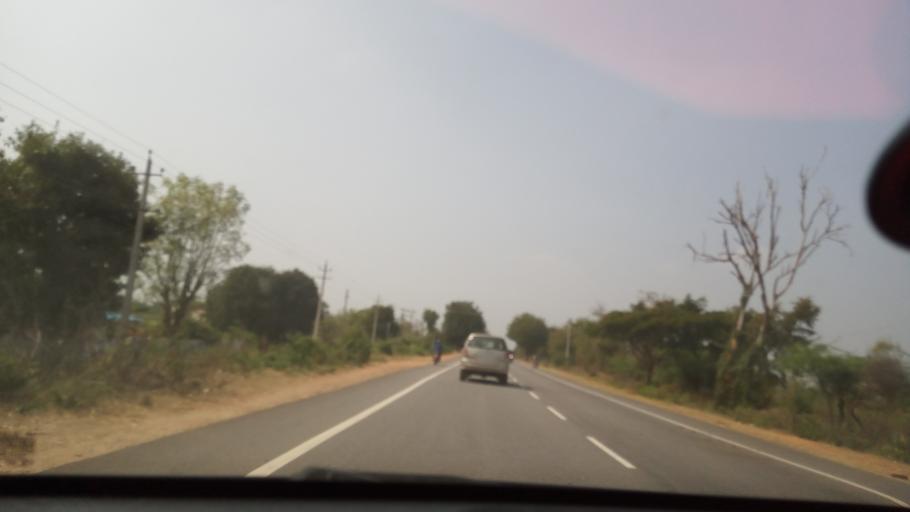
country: IN
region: Karnataka
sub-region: Mysore
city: Nanjangud
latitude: 12.0710
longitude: 76.7451
